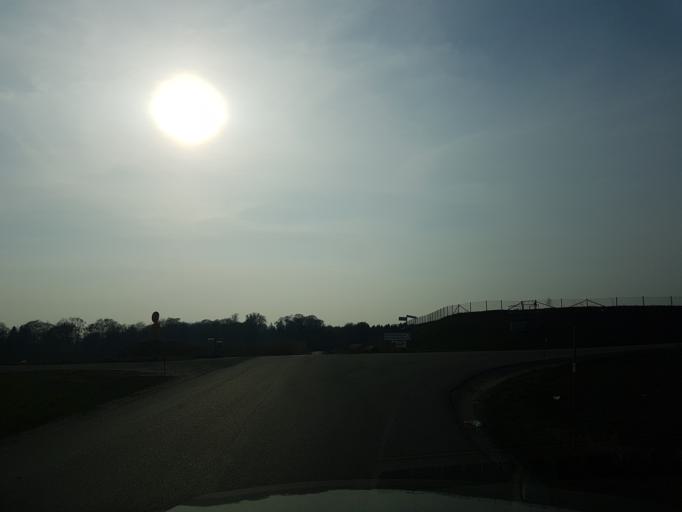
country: SE
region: Skane
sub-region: Ystads Kommun
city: Ystad
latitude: 55.4598
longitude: 13.7882
